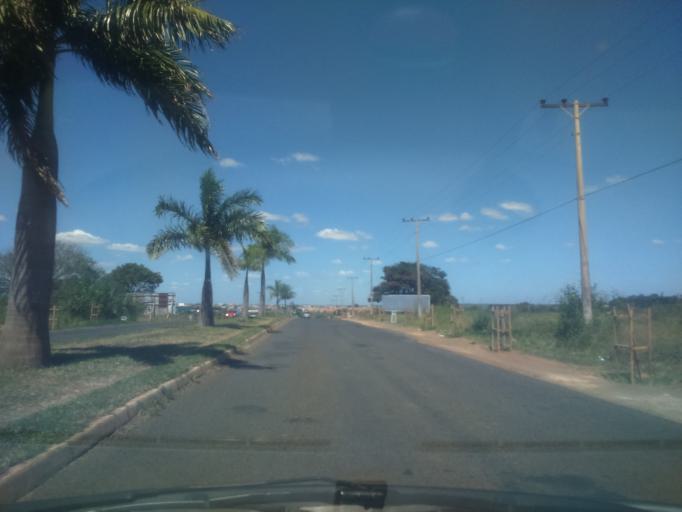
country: BR
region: Goias
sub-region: Luziania
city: Luziania
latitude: -16.1056
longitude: -47.9464
